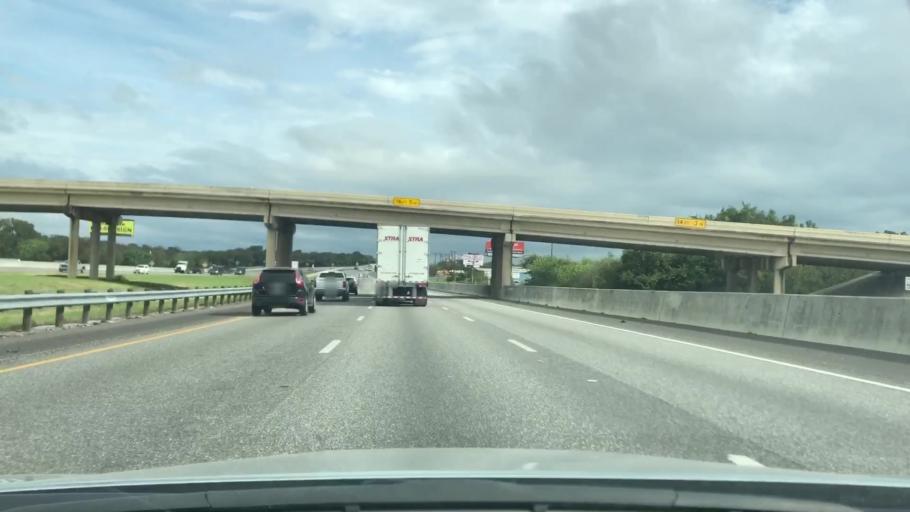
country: US
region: Texas
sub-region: Guadalupe County
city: Redwood
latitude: 29.7929
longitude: -98.0225
